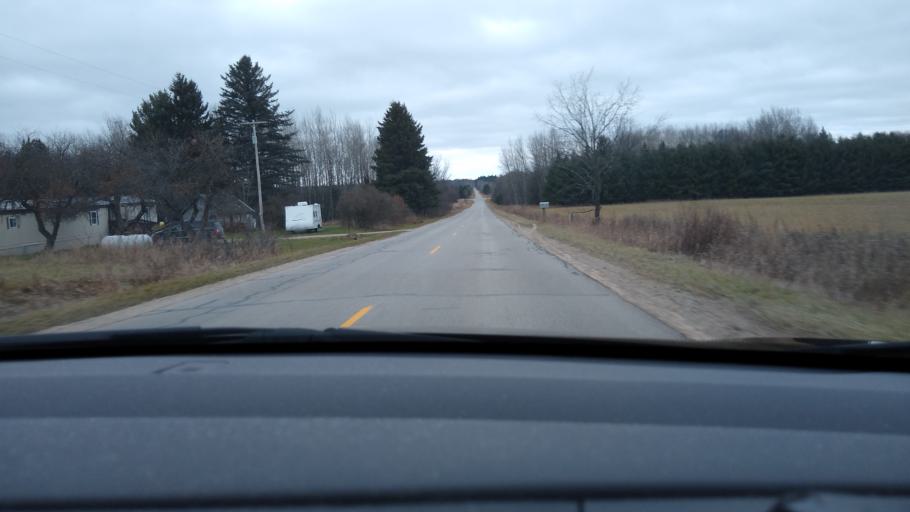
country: US
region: Michigan
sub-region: Missaukee County
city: Lake City
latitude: 44.3317
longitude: -85.0550
